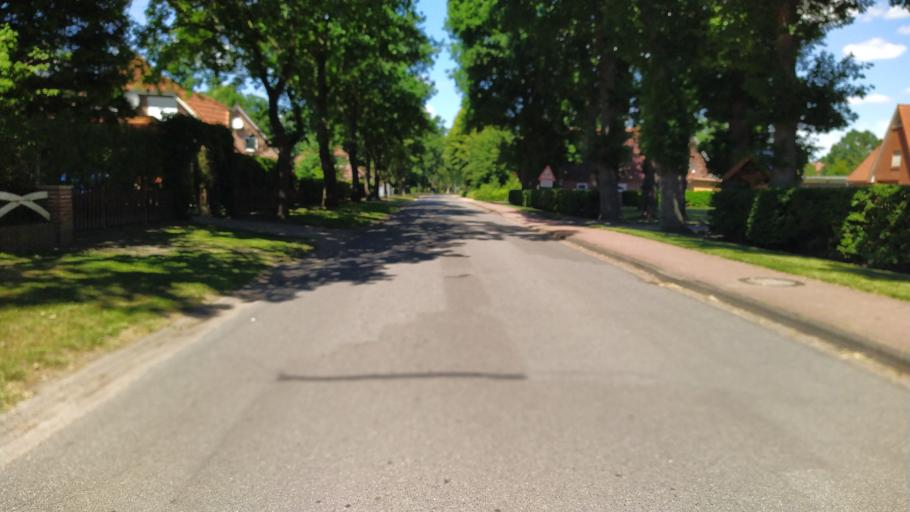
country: DE
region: Lower Saxony
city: Estorf
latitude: 53.5735
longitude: 9.2034
